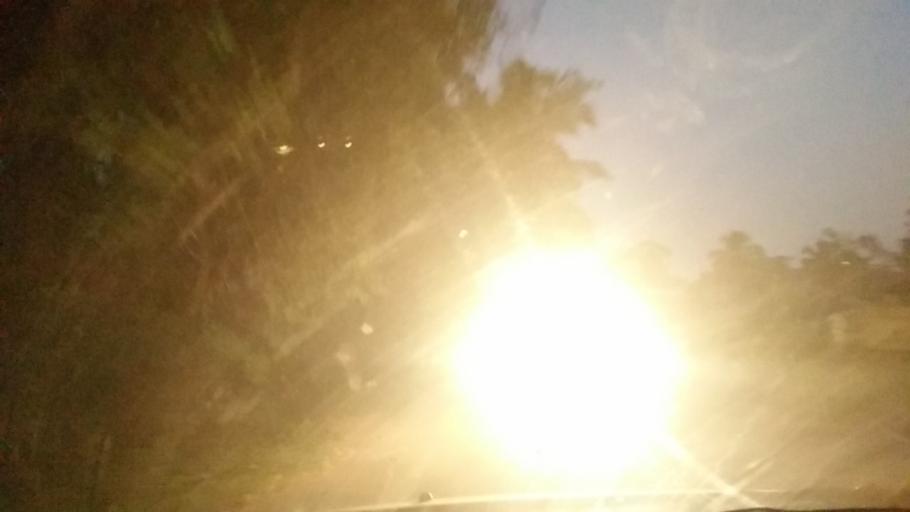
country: IN
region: Goa
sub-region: South Goa
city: Madgaon
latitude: 15.2649
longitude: 73.9647
